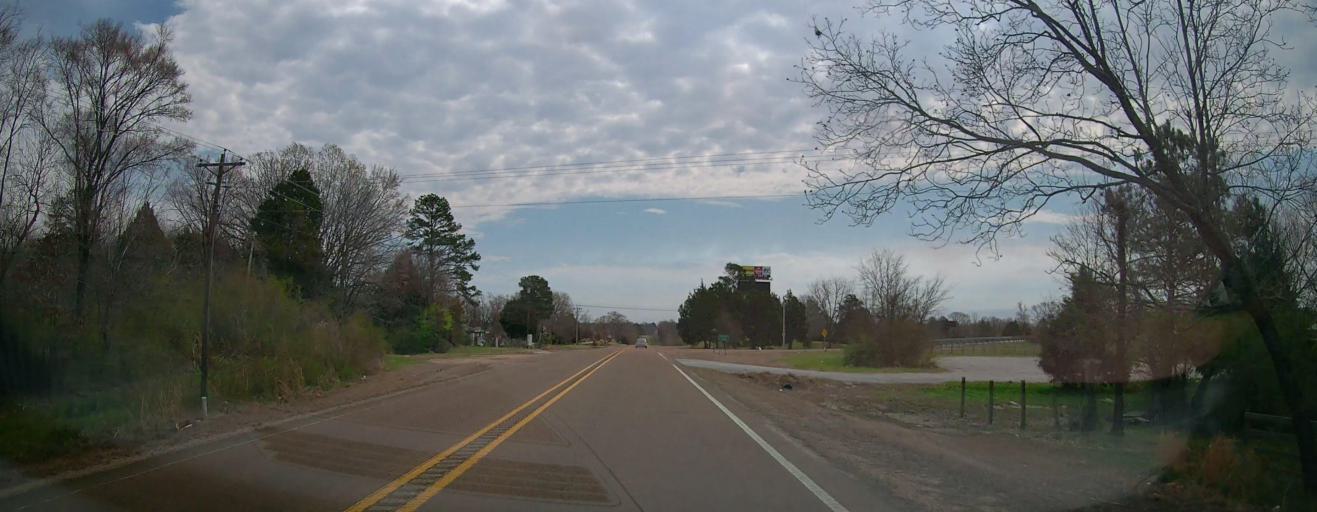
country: US
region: Mississippi
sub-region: Marshall County
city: Holly Springs
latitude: 34.8094
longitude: -89.5146
